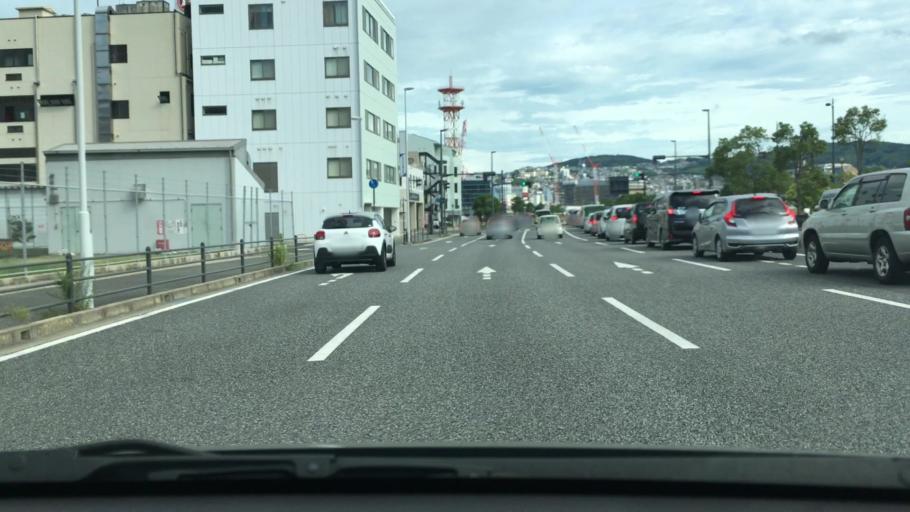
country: JP
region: Nagasaki
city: Nagasaki-shi
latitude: 32.7577
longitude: 129.8646
